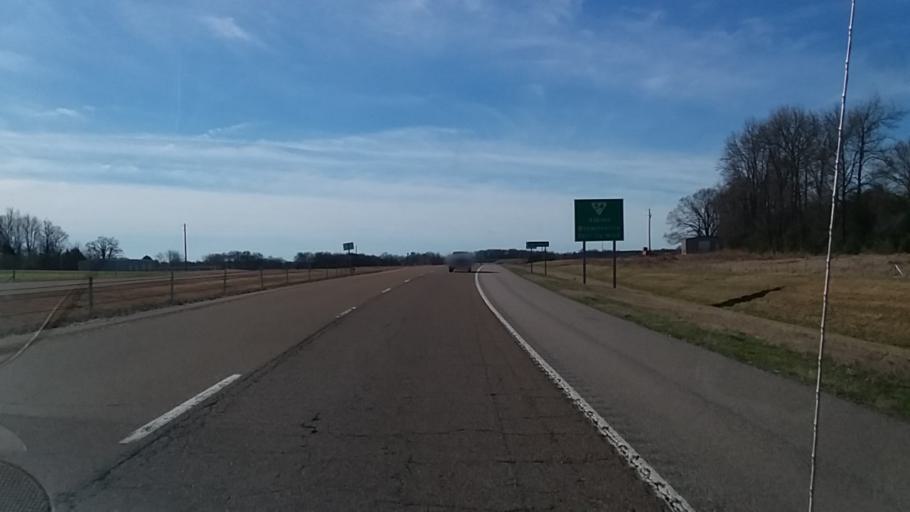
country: US
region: Tennessee
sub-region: Crockett County
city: Alamo
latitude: 35.8108
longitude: -89.1608
